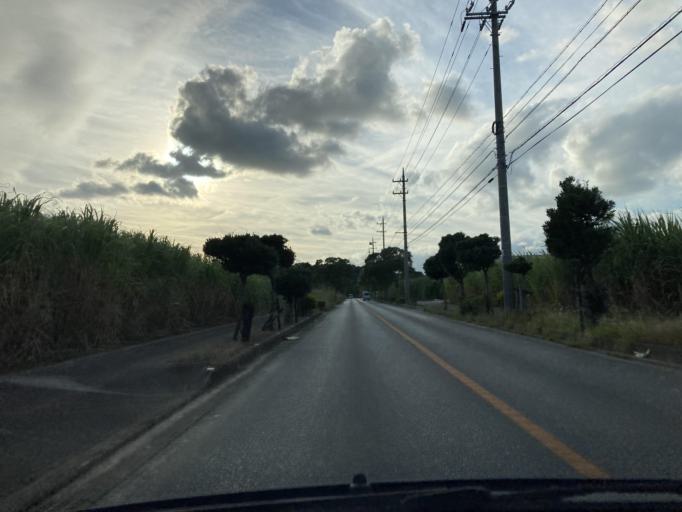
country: JP
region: Okinawa
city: Itoman
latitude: 26.1351
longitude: 127.7037
